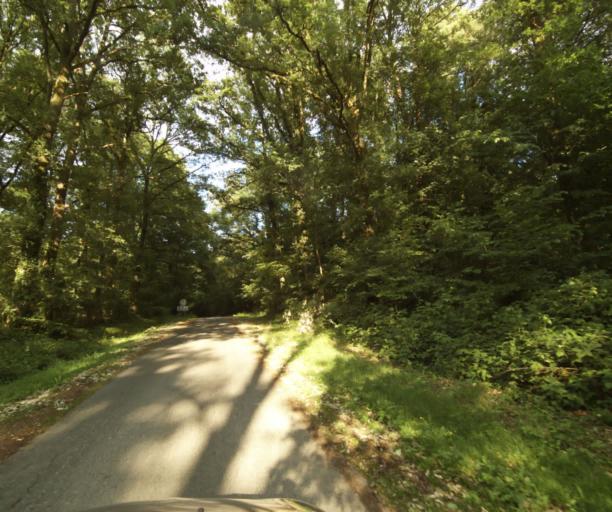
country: FR
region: Champagne-Ardenne
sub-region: Departement des Ardennes
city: Warcq
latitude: 49.8131
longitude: 4.6972
